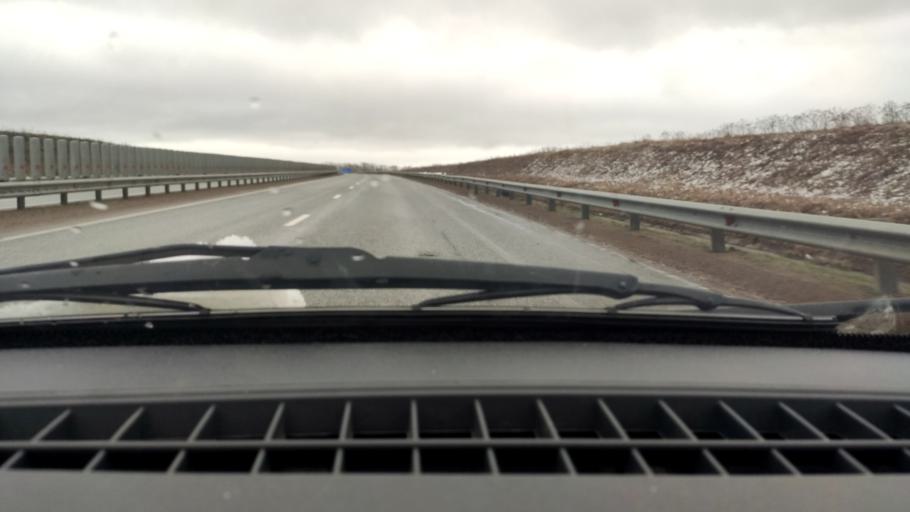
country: RU
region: Bashkortostan
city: Kushnarenkovo
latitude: 55.0667
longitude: 55.3050
